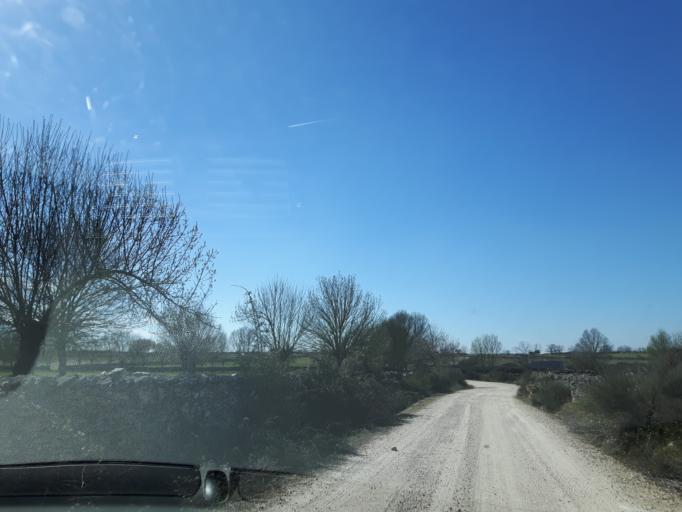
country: ES
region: Castille and Leon
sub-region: Provincia de Salamanca
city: Bermellar
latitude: 40.9624
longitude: -6.6787
